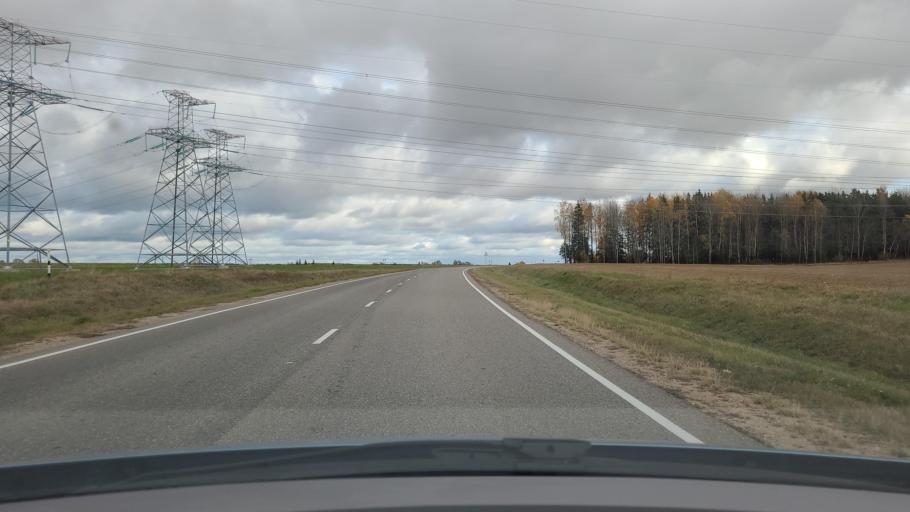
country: BY
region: Grodnenskaya
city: Astravyets
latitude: 54.7664
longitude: 26.0758
